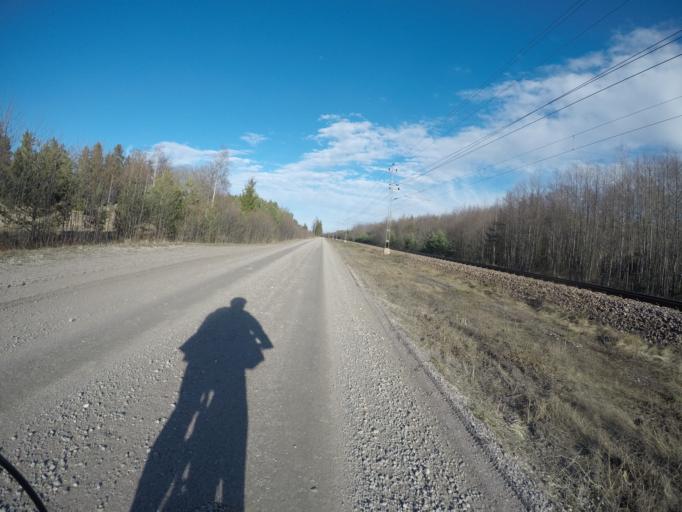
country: SE
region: Soedermanland
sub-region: Eskilstuna Kommun
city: Kvicksund
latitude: 59.4236
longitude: 16.3054
